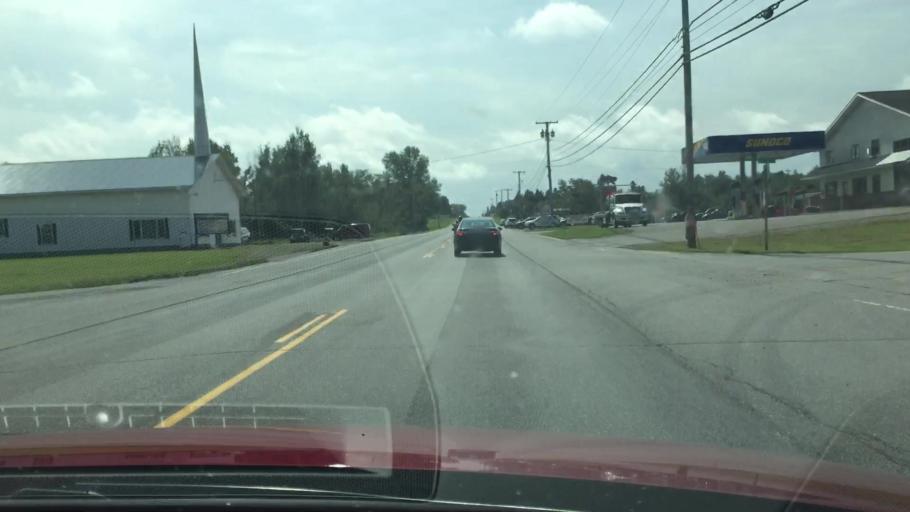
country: US
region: Maine
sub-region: Aroostook County
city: Houlton
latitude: 46.2419
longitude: -67.8409
